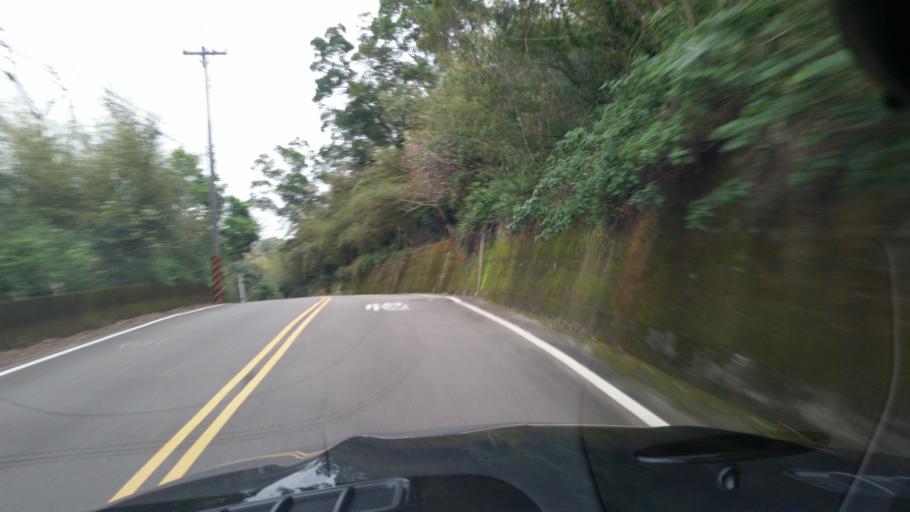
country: TW
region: Taiwan
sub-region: Miaoli
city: Miaoli
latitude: 24.5802
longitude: 120.8862
